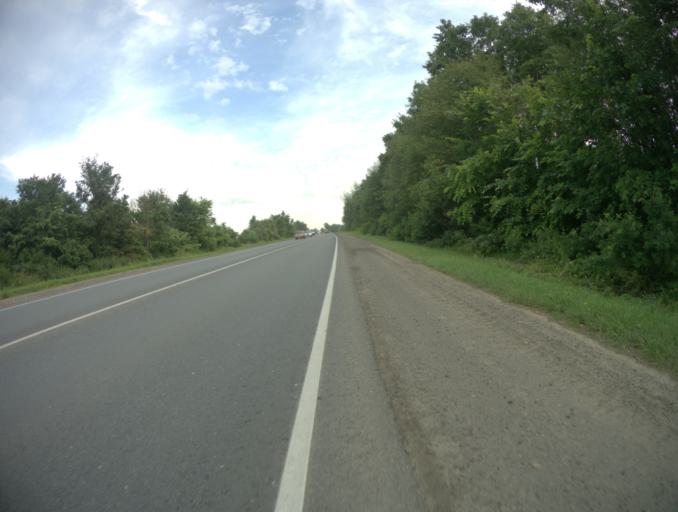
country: RU
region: Vladimir
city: Suzdal'
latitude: 56.3790
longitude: 40.4576
